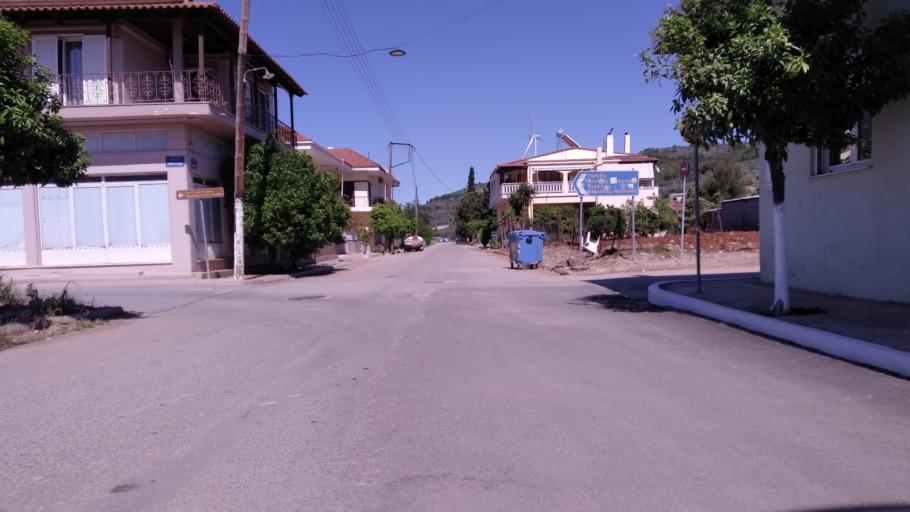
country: GR
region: Central Greece
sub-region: Nomos Fthiotidos
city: Malesina
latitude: 38.6239
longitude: 23.2386
